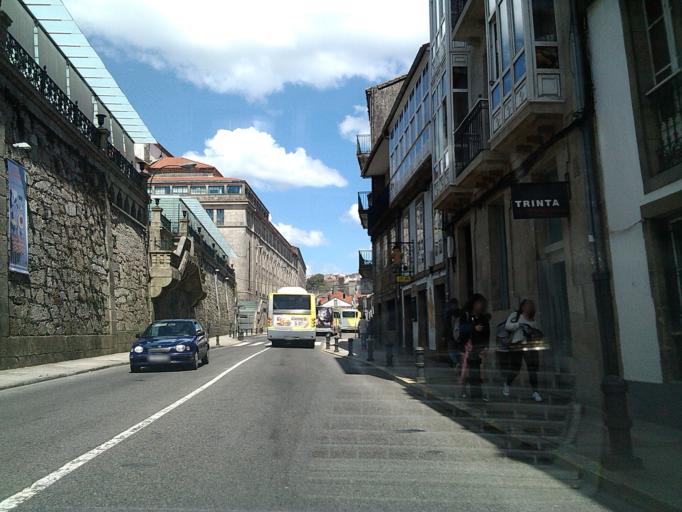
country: ES
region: Galicia
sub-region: Provincia da Coruna
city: Santiago de Compostela
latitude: 42.8796
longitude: -8.5410
